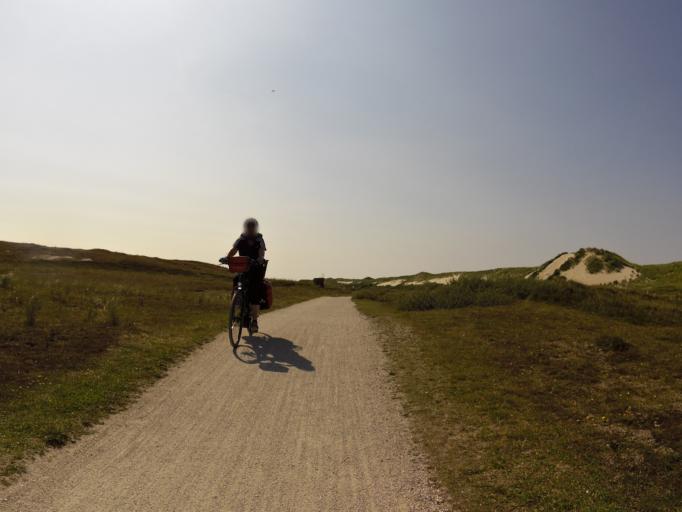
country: NL
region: North Holland
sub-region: Gemeente Schagen
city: Harenkarspel
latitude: 52.7872
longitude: 4.6712
